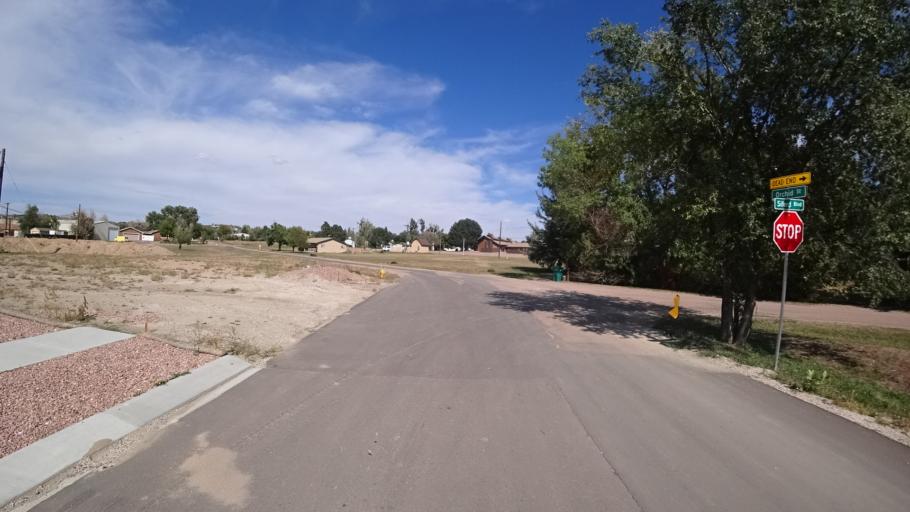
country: US
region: Colorado
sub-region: El Paso County
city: Cimarron Hills
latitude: 38.8927
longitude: -104.7486
